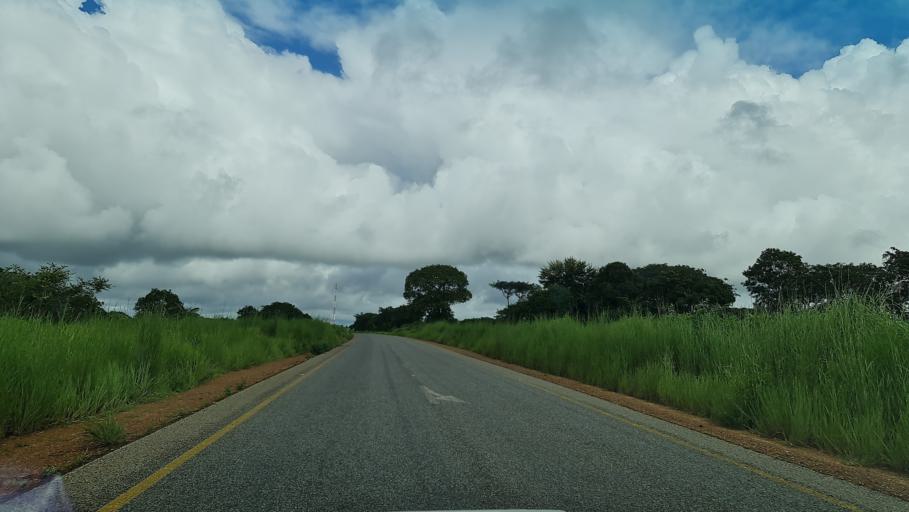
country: MZ
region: Nampula
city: Nampula
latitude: -15.0311
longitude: 38.4459
